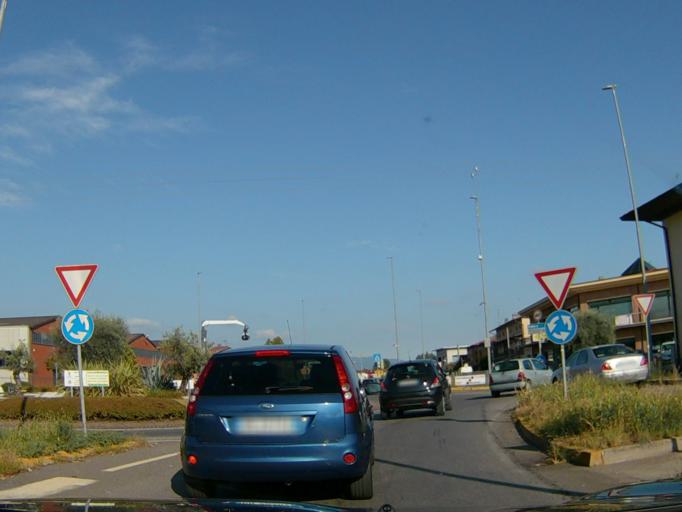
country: IT
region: Lombardy
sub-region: Provincia di Brescia
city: Lodetto
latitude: 45.5582
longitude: 10.0409
